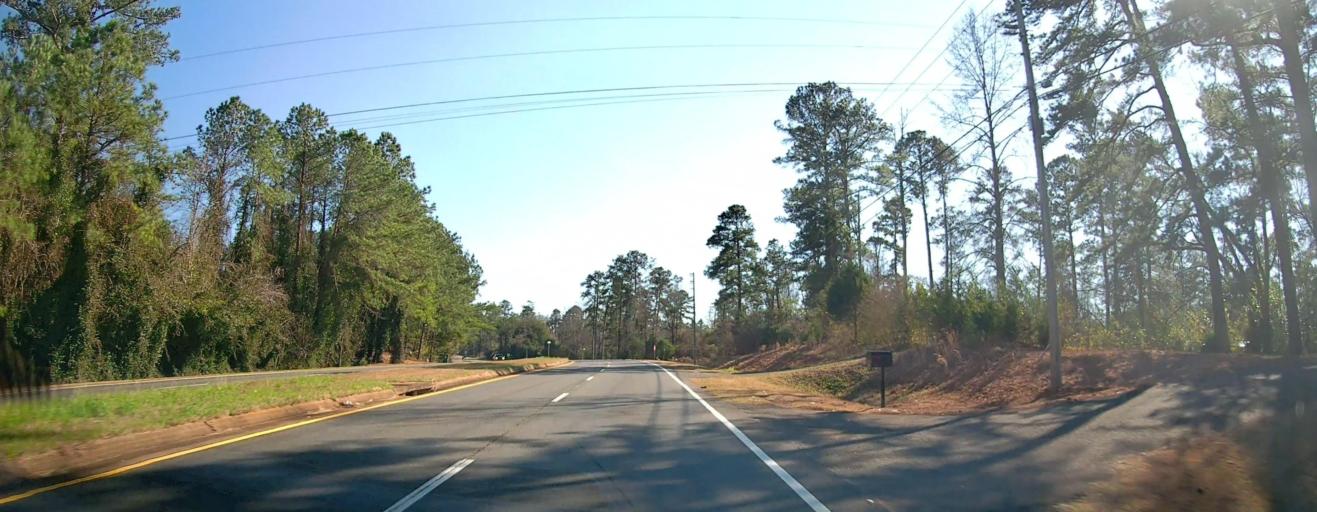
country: US
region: Georgia
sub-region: Sumter County
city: Americus
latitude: 32.1020
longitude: -84.2444
